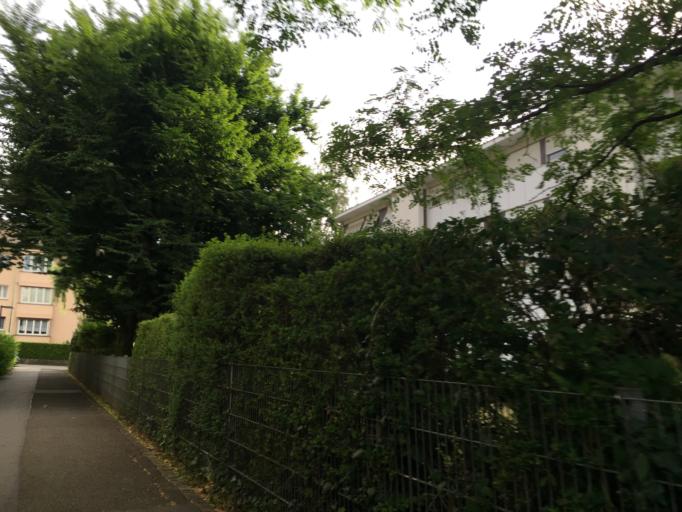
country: CH
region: Bern
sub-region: Bern-Mittelland District
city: Koniz
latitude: 46.9312
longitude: 7.4273
